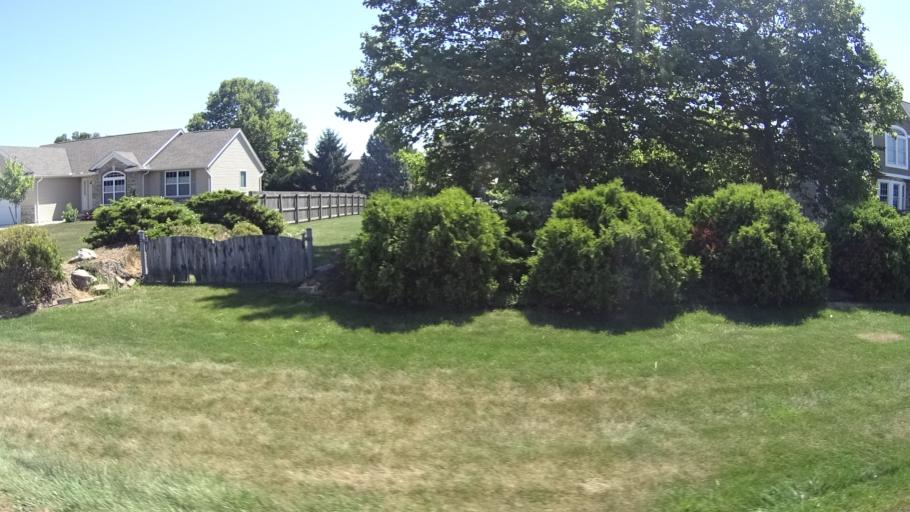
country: US
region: Ohio
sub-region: Erie County
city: Sandusky
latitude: 41.4185
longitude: -82.7032
